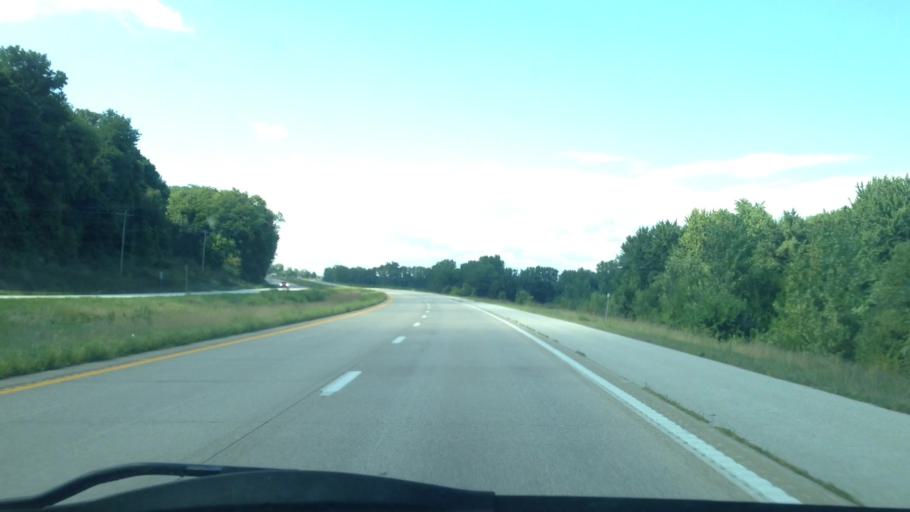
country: US
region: Missouri
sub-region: Lewis County
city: Canton
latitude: 40.2364
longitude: -91.5333
